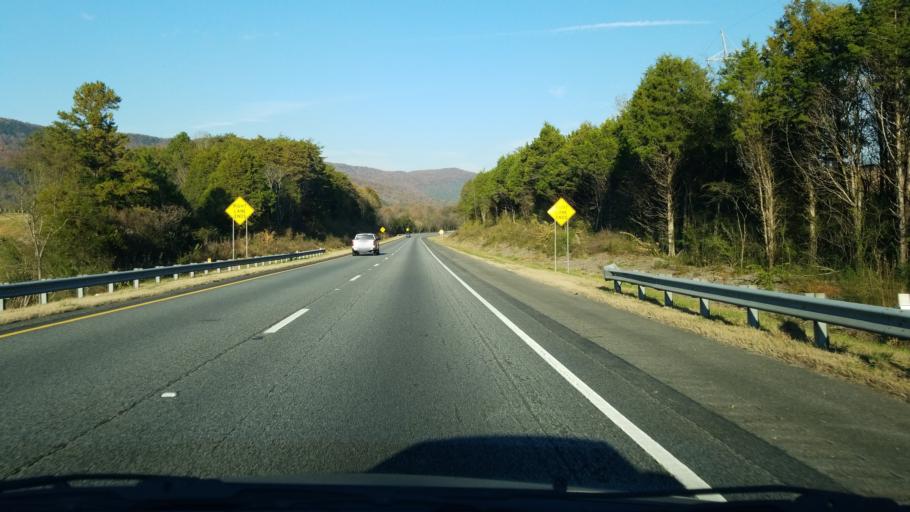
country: US
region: Georgia
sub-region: Walker County
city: Lookout Mountain
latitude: 34.9669
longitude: -85.4514
